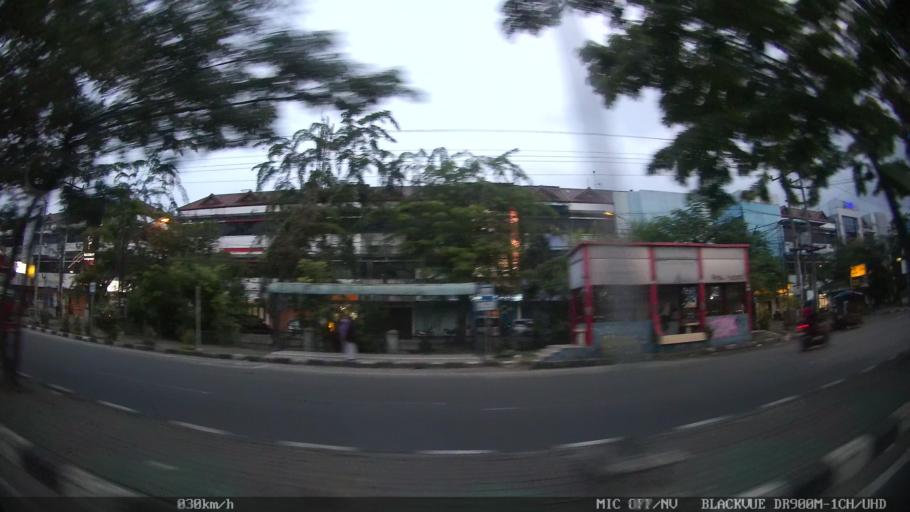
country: ID
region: North Sumatra
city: Medan
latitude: 3.5908
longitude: 98.6418
